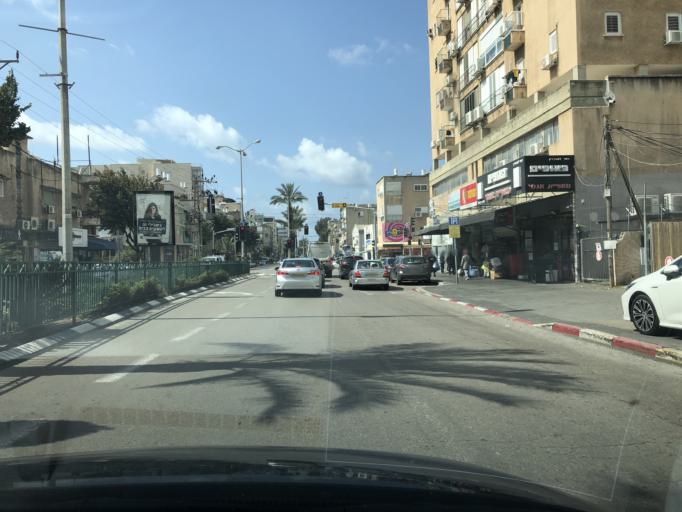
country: IL
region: Haifa
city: Hadera
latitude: 32.4395
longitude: 34.9207
